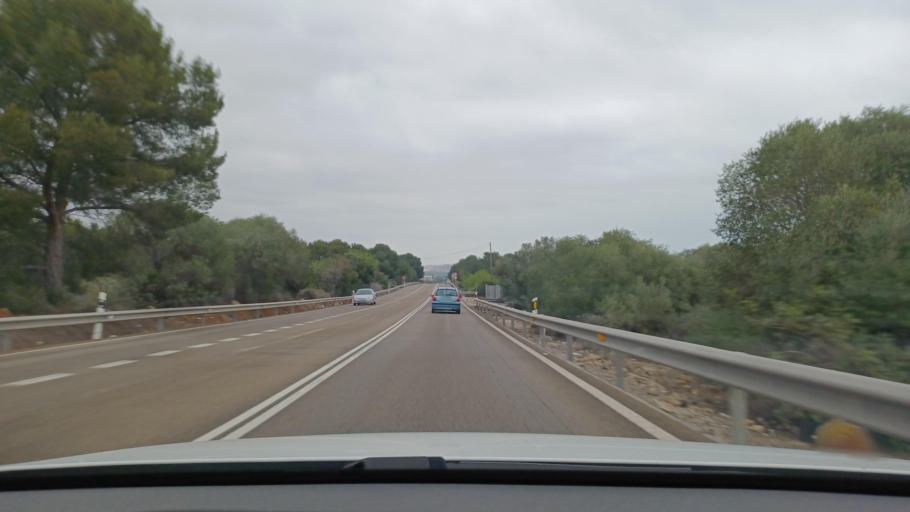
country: ES
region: Valencia
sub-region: Provincia de Castello
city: Orpesa/Oropesa del Mar
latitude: 40.0837
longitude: 0.1203
